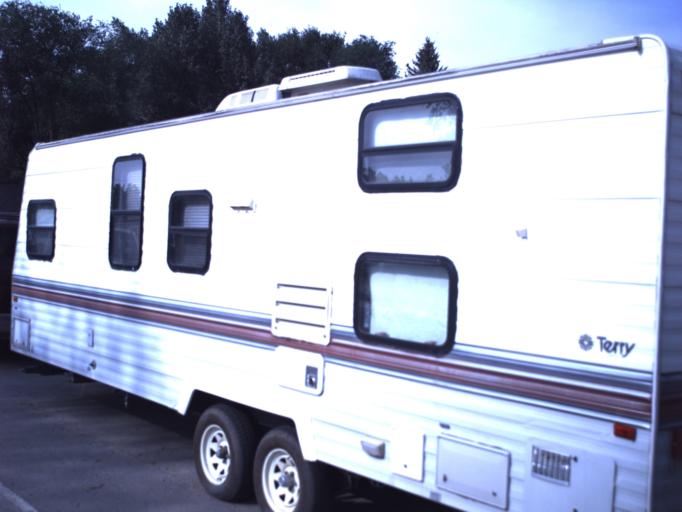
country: US
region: Utah
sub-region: Duchesne County
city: Duchesne
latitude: 40.1662
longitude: -110.4014
